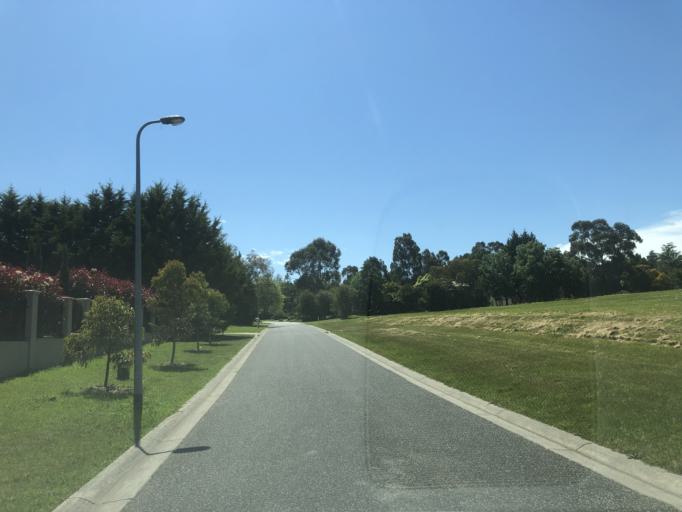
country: AU
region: Victoria
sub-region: Casey
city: Endeavour Hills
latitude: -37.9846
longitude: 145.2808
